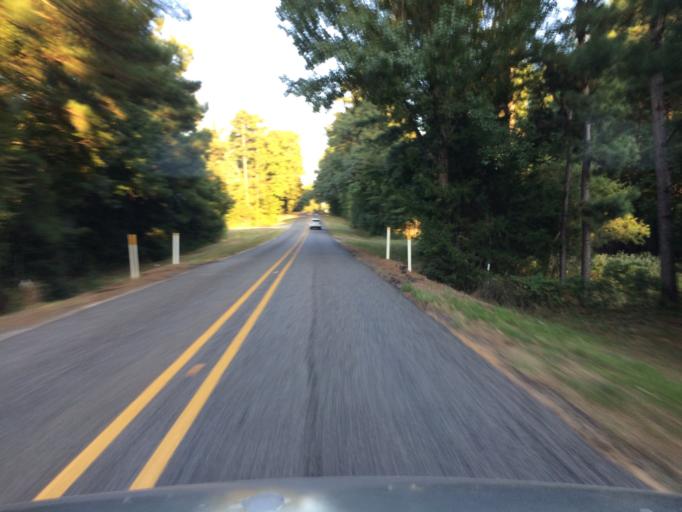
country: US
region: Texas
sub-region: Wood County
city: Hawkins
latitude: 32.7345
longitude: -95.2439
